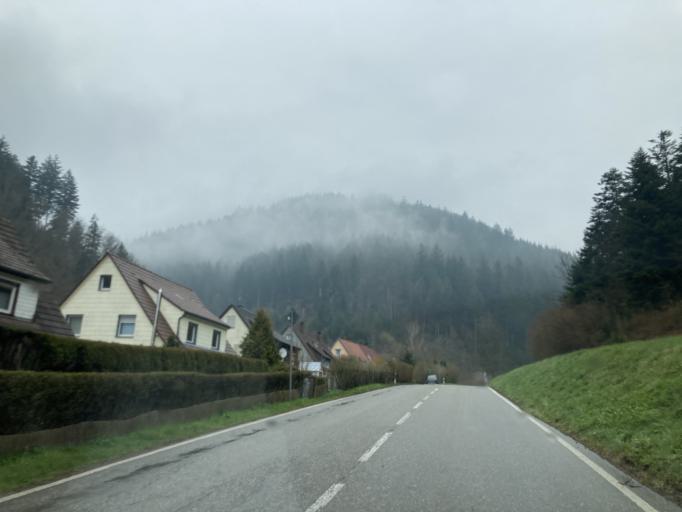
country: DE
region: Baden-Wuerttemberg
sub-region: Freiburg Region
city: Hornberg
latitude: 48.2192
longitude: 8.2458
